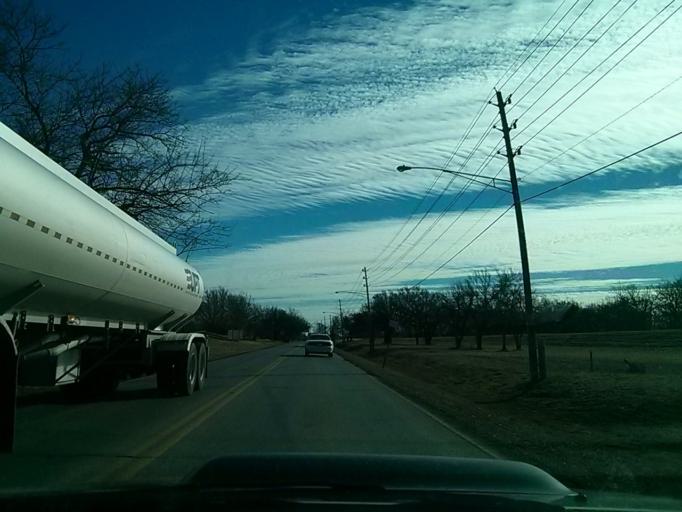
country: US
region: Oklahoma
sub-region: Tulsa County
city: Jenks
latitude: 36.0245
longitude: -95.9931
